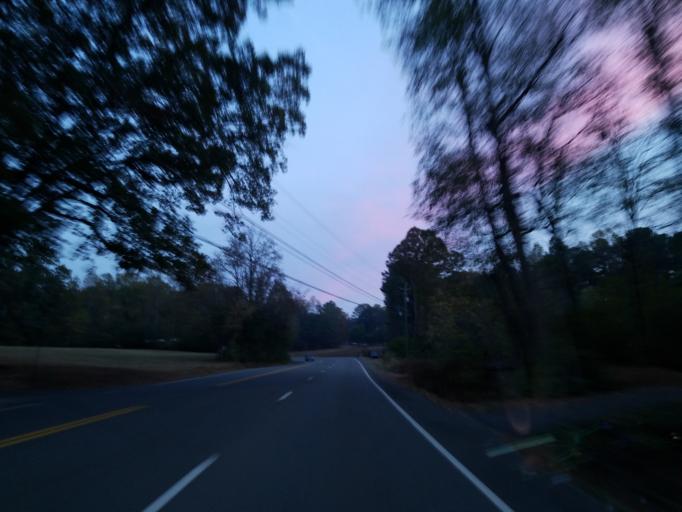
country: US
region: Georgia
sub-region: Pickens County
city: Jasper
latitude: 34.4949
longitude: -84.4694
